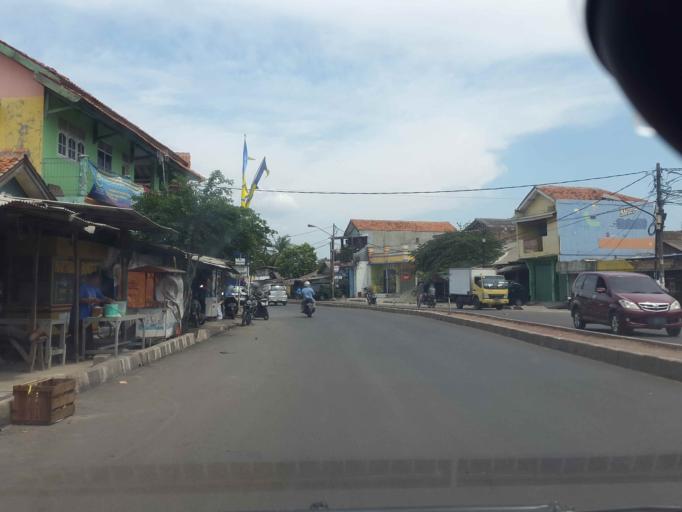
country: ID
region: Banten
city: Tangerang
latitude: -6.1555
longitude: 106.6642
